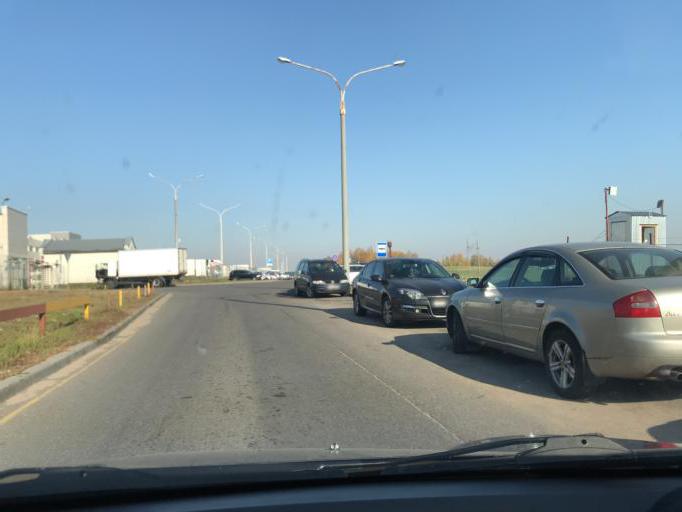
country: BY
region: Minsk
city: Pryvol'ny
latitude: 53.8136
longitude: 27.7866
